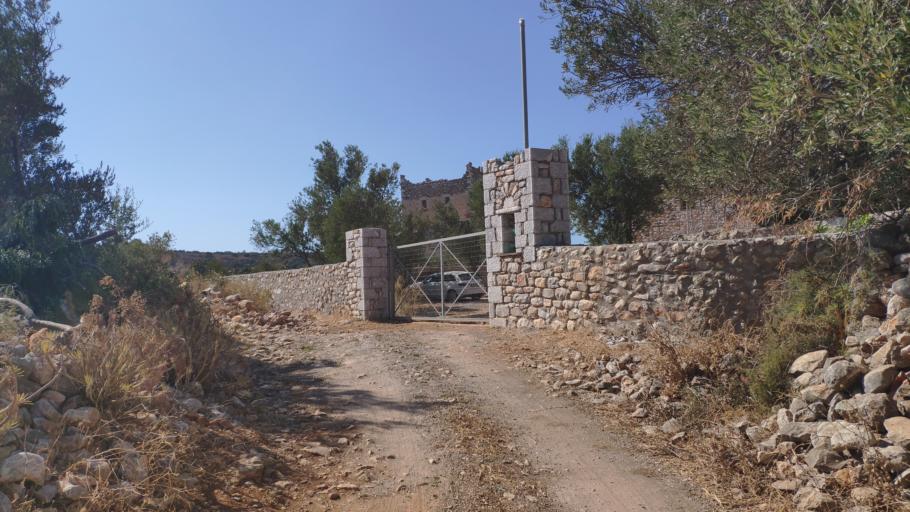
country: GR
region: Peloponnese
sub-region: Nomos Lakonias
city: Gytheio
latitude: 36.5139
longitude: 22.3939
